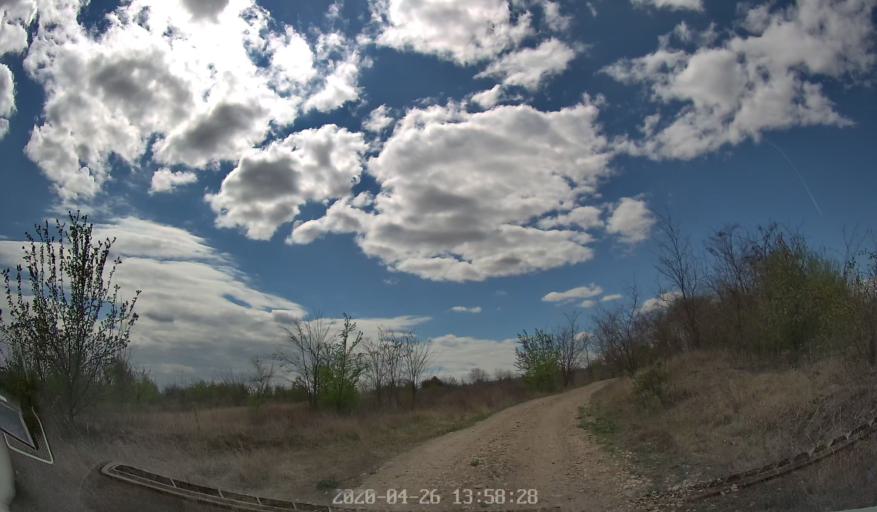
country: MD
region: Telenesti
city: Cocieri
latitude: 47.2687
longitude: 29.1208
